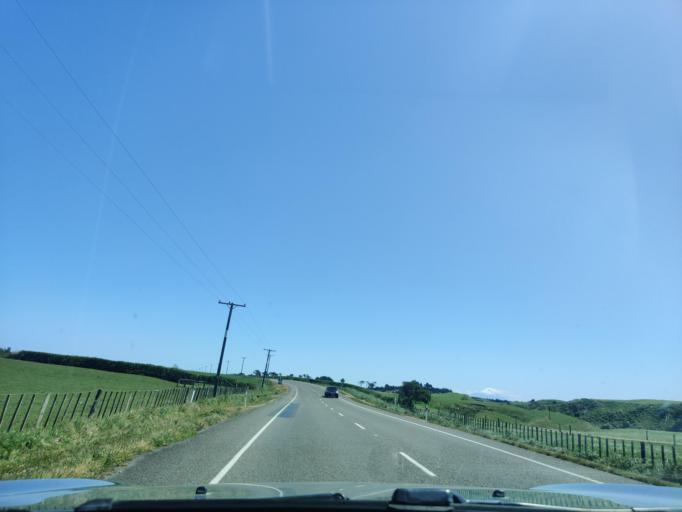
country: NZ
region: Taranaki
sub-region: South Taranaki District
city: Patea
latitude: -39.7491
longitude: 174.5356
